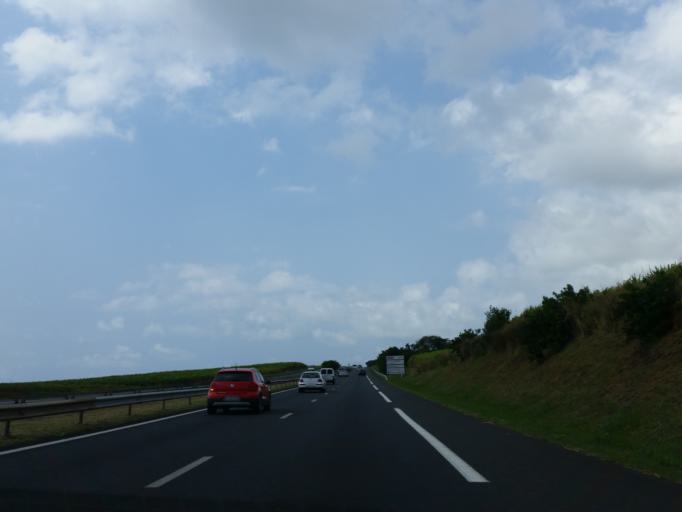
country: RE
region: Reunion
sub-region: Reunion
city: Sainte-Suzanne
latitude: -20.8999
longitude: 55.5843
